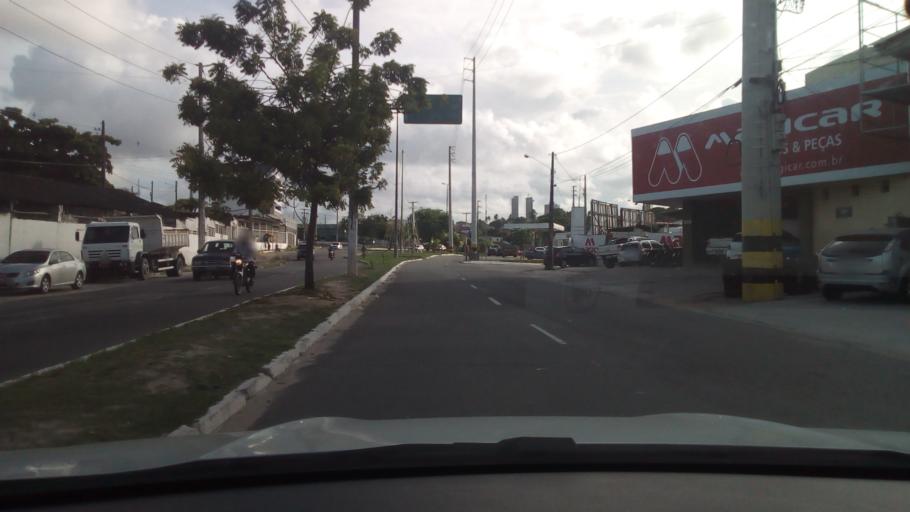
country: BR
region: Paraiba
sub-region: Joao Pessoa
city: Joao Pessoa
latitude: -7.0988
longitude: -34.8597
